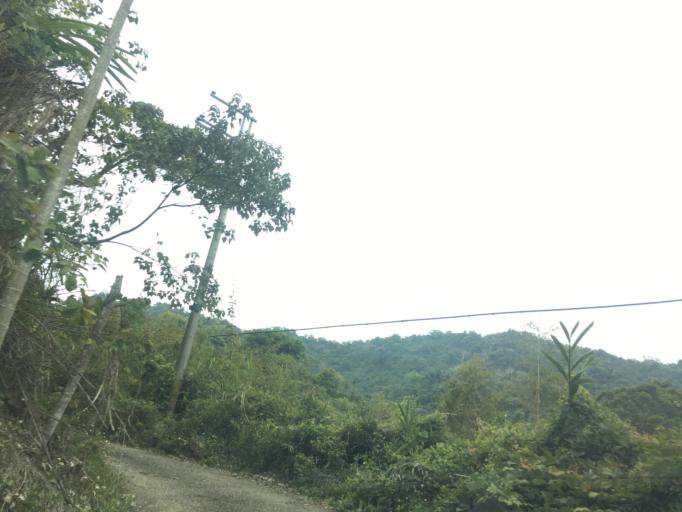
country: TW
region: Taiwan
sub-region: Taichung City
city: Taichung
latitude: 24.1348
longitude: 120.8250
